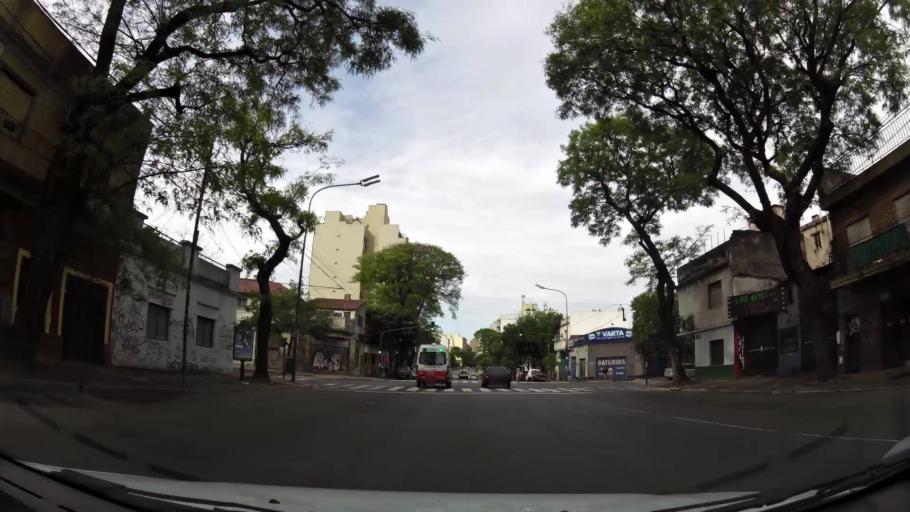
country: AR
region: Buenos Aires F.D.
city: Villa Santa Rita
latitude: -34.6399
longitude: -58.4777
